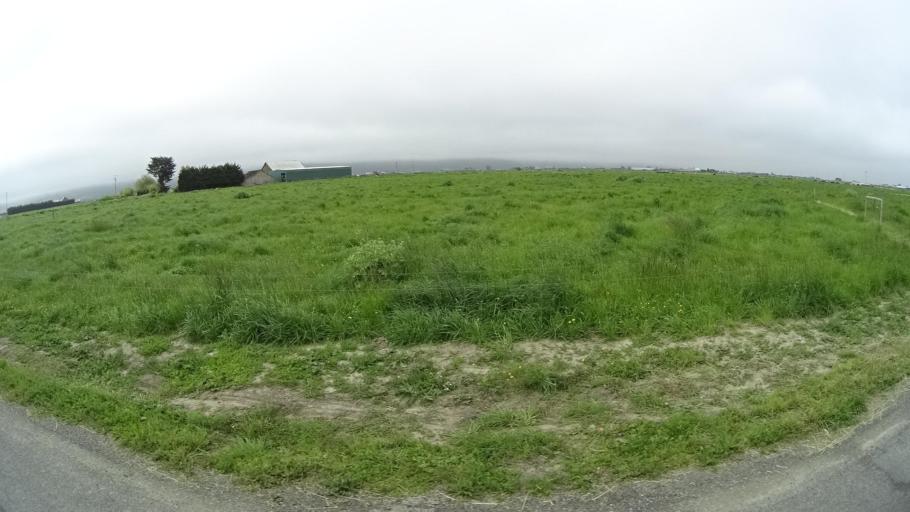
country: US
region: California
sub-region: Humboldt County
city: Fortuna
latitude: 40.5905
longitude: -124.1888
